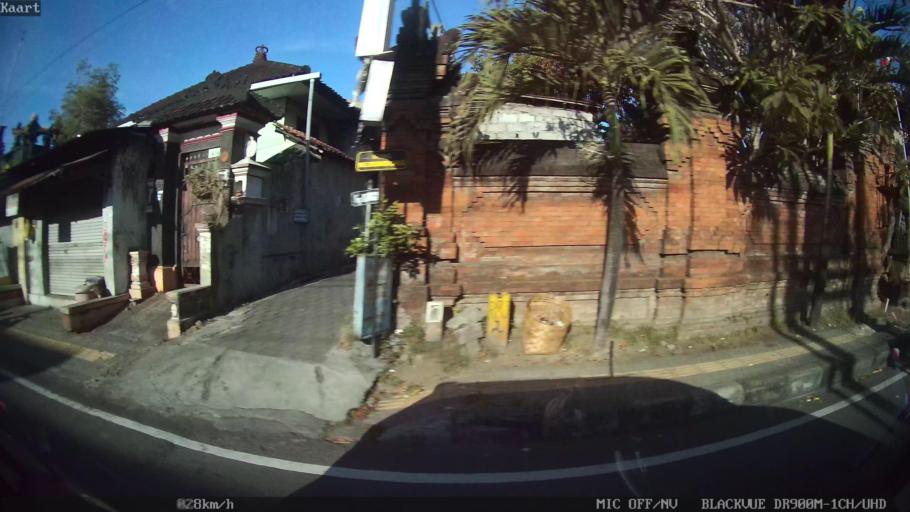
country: ID
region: Bali
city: Banjar Kertasari
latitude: -8.6248
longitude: 115.2008
